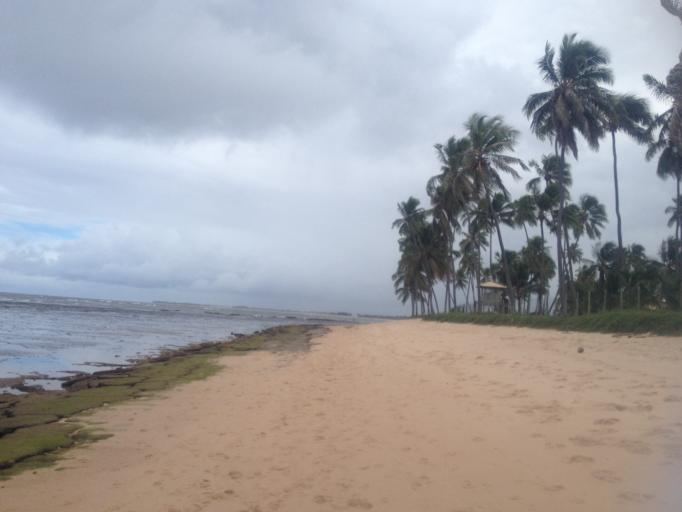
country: BR
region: Bahia
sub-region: Mata De Sao Joao
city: Mata de Sao Joao
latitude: -12.5811
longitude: -38.0068
